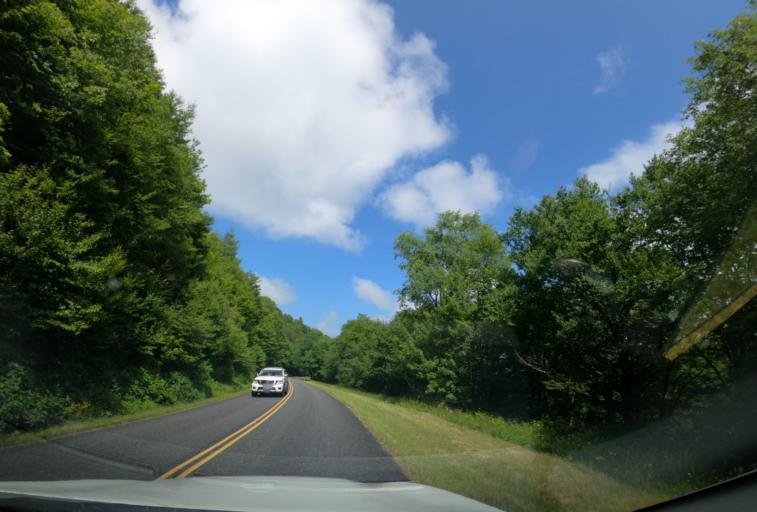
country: US
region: North Carolina
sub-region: Haywood County
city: Hazelwood
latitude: 35.3959
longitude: -83.0398
